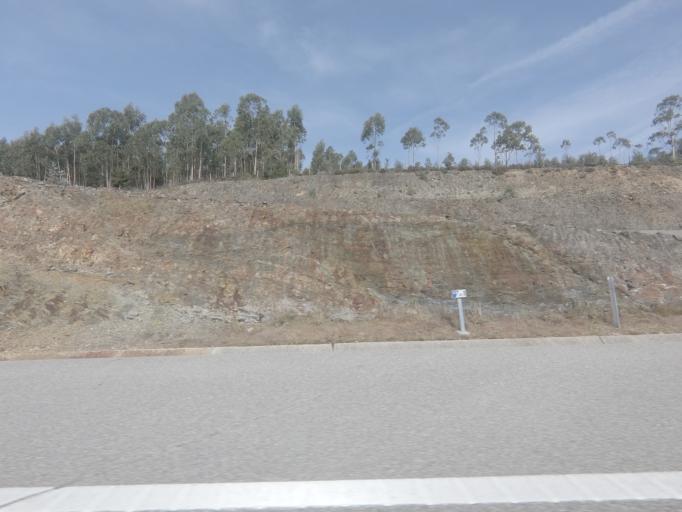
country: PT
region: Aveiro
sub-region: Agueda
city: Valongo
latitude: 40.6522
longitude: -8.3769
